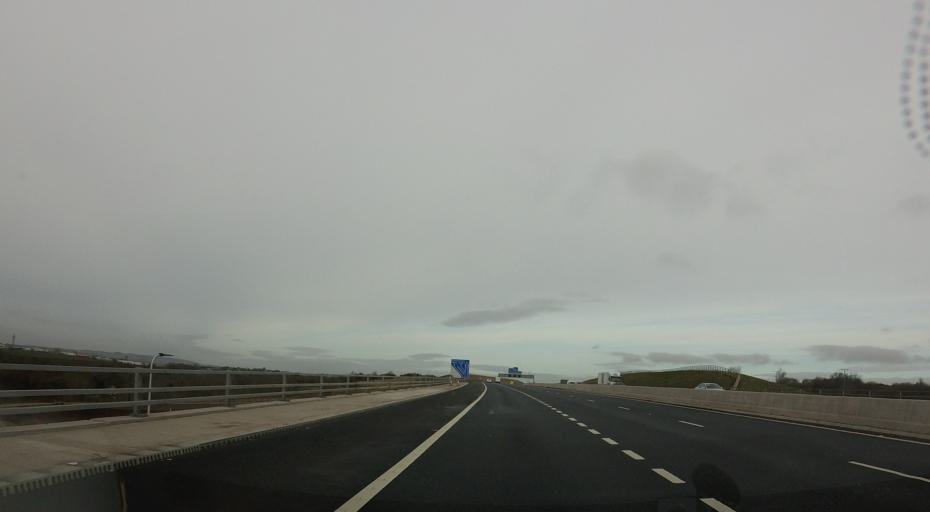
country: GB
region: Scotland
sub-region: South Lanarkshire
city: Uddingston
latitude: 55.8464
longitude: -4.0672
